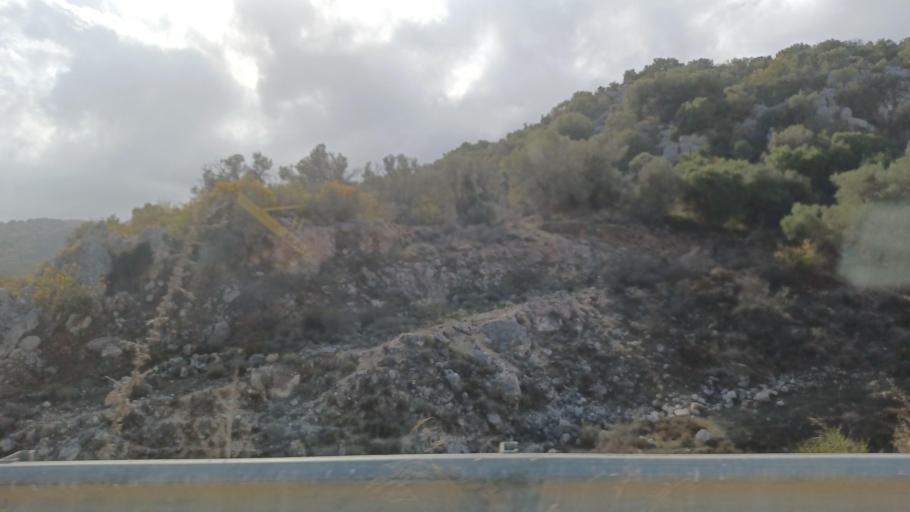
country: CY
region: Pafos
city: Polis
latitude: 34.9982
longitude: 32.4013
